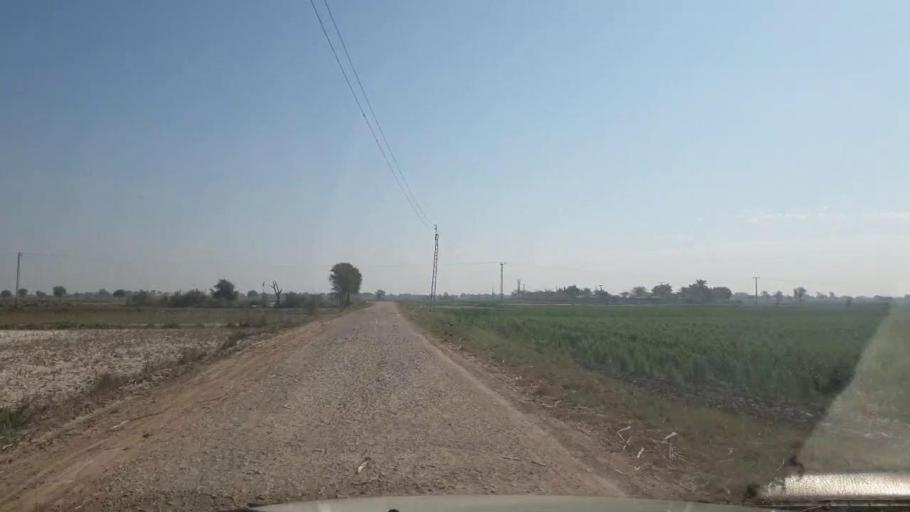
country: PK
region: Sindh
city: Mirpur Khas
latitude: 25.5101
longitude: 69.1480
